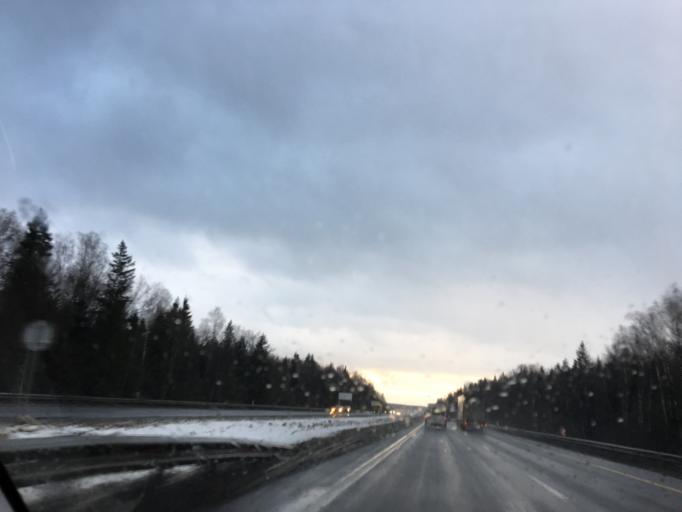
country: RU
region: Moskovskaya
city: Danki
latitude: 54.9649
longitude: 37.5291
